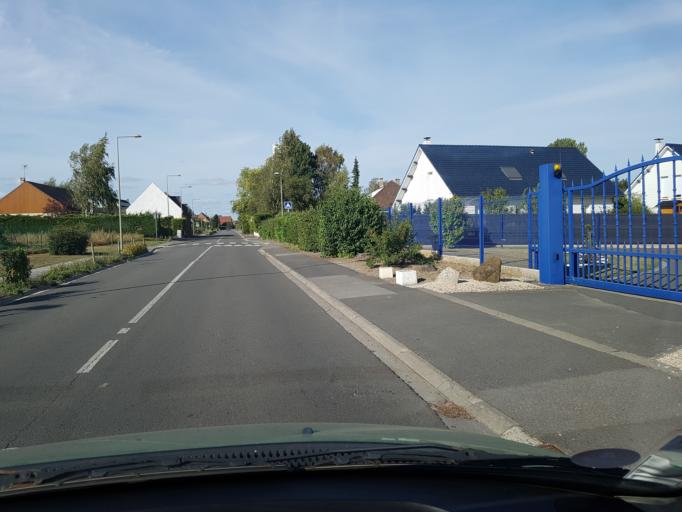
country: FR
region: Nord-Pas-de-Calais
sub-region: Departement du Pas-de-Calais
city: Hinges
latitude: 50.5581
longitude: 2.6187
